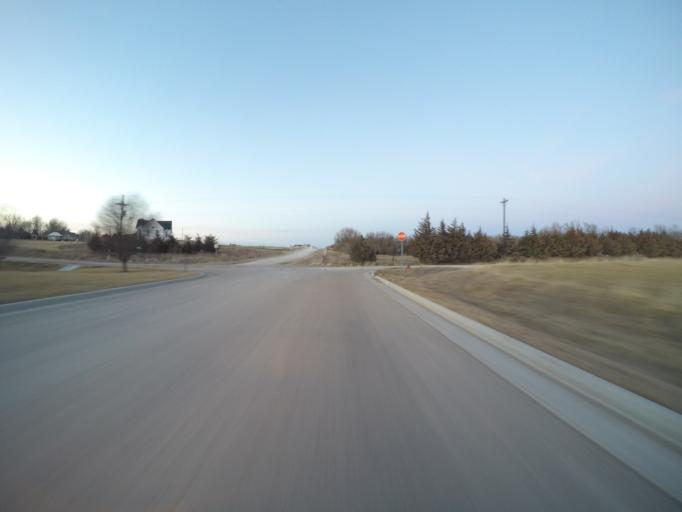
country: US
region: Kansas
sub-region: Clay County
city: Clay Center
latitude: 39.3935
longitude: -97.1186
